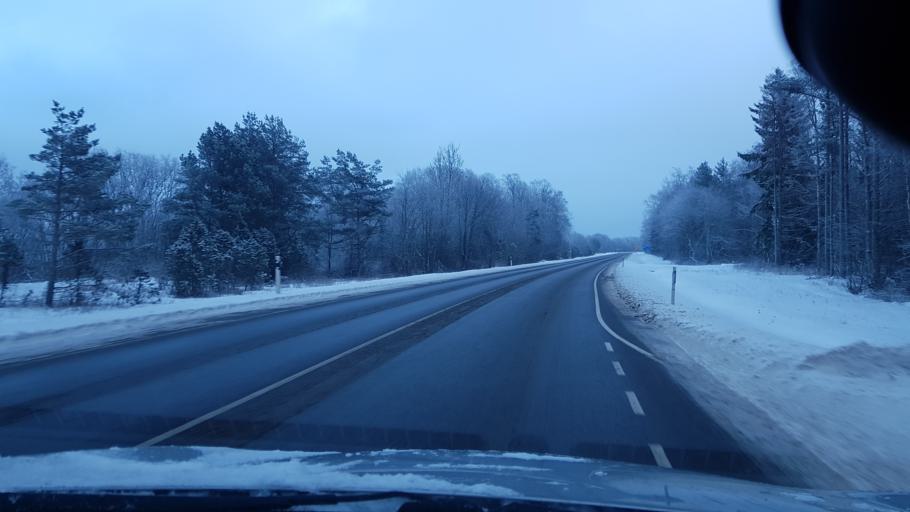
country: EE
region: Harju
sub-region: Paldiski linn
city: Paldiski
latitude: 59.3449
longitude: 24.1854
